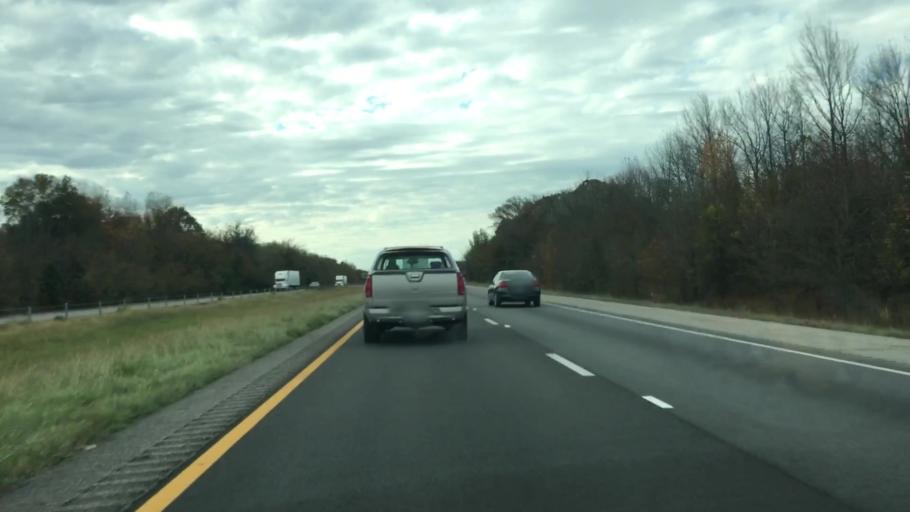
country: US
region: Arkansas
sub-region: Conway County
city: Morrilton
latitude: 35.1621
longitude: -92.6095
